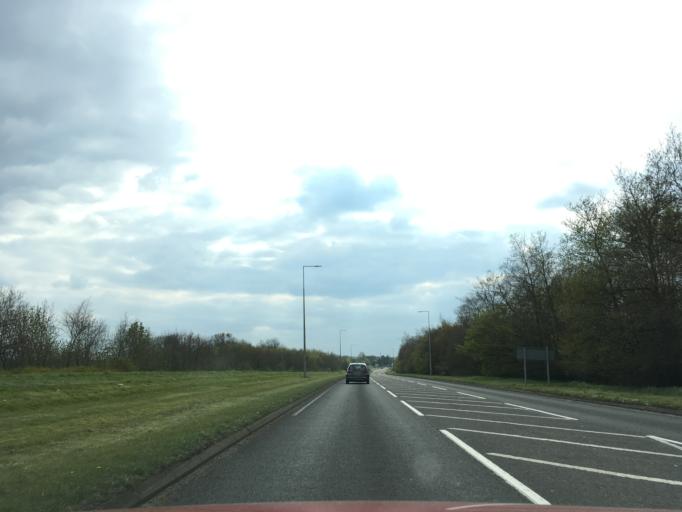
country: GB
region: England
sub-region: Milton Keynes
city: Loughton
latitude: 52.0164
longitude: -0.7711
